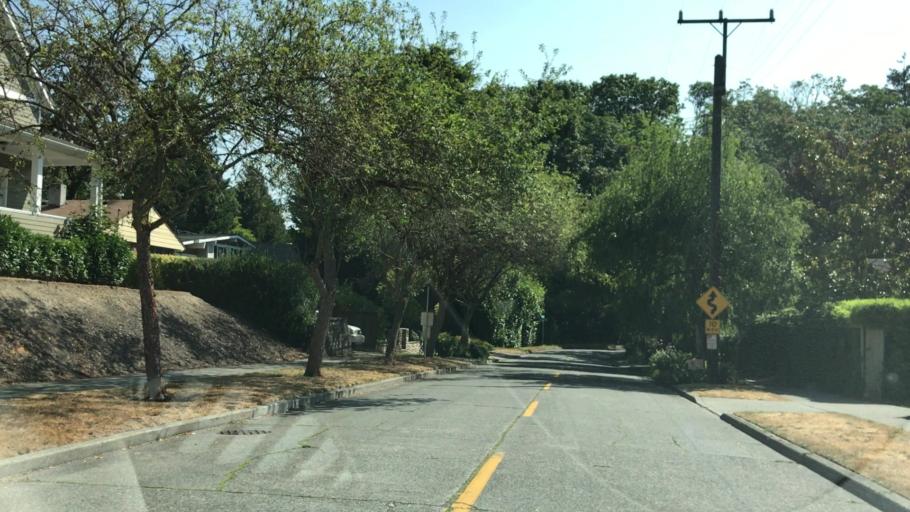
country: US
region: Washington
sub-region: King County
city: Seattle
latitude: 47.6009
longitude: -122.2913
